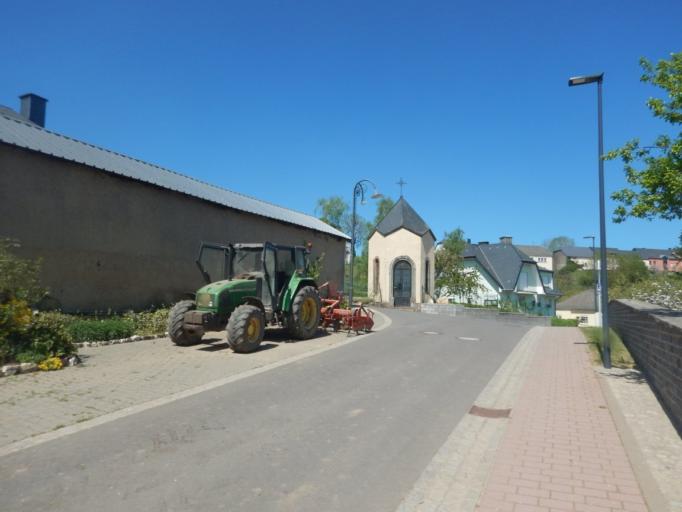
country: LU
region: Diekirch
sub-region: Canton de Diekirch
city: Bourscheid
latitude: 49.9078
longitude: 6.0621
